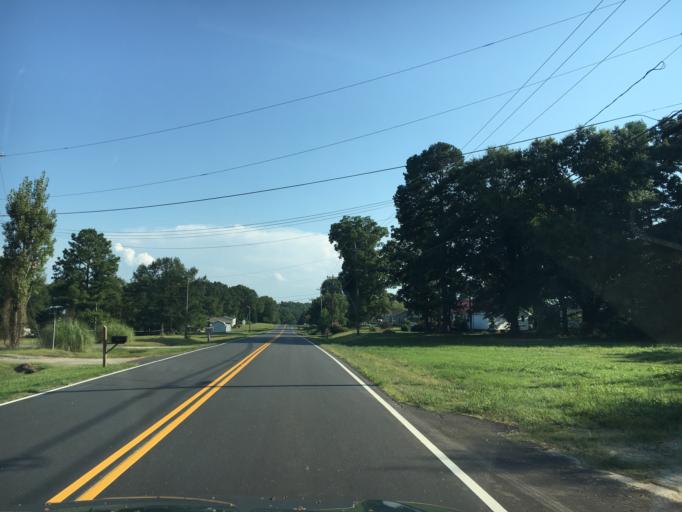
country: US
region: South Carolina
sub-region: Spartanburg County
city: Duncan
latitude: 34.9155
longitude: -82.1448
